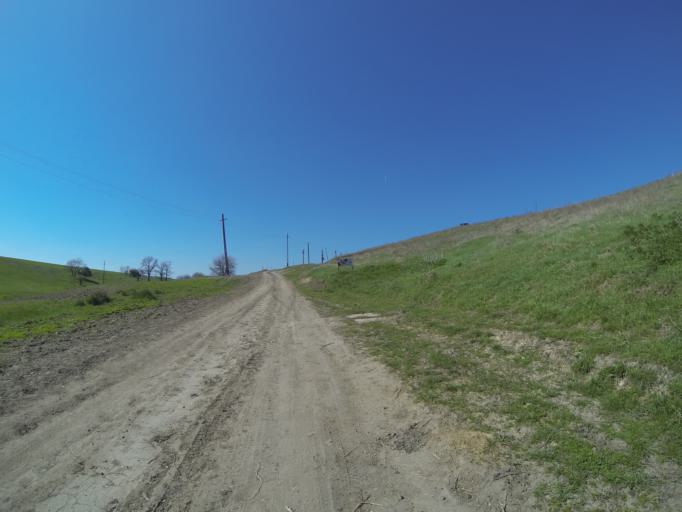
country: RO
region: Dolj
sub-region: Comuna Caloparu
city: Salcuta
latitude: 44.1590
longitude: 23.6683
